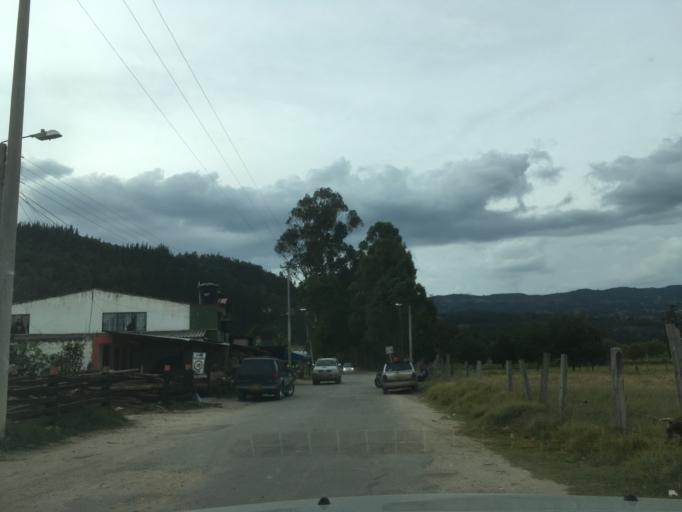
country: CO
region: Boyaca
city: Firavitoba
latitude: 5.6699
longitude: -72.9973
